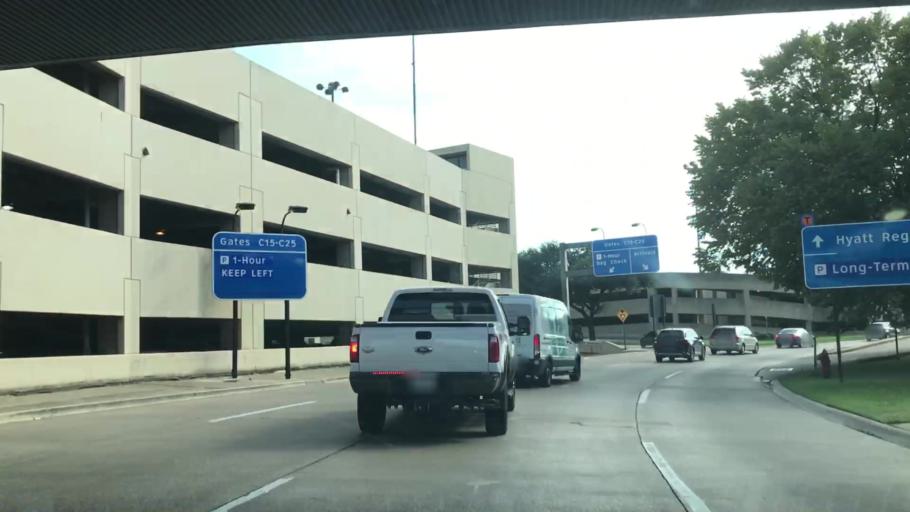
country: US
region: Texas
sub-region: Tarrant County
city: Grapevine
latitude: 32.8976
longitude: -97.0372
